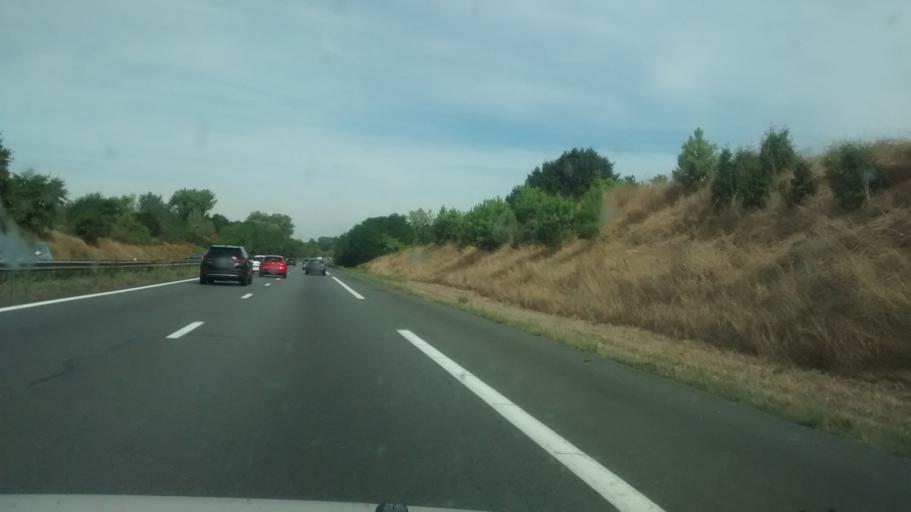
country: FR
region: Aquitaine
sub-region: Departement de la Gironde
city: Cadaujac
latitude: 44.7534
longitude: -0.5431
